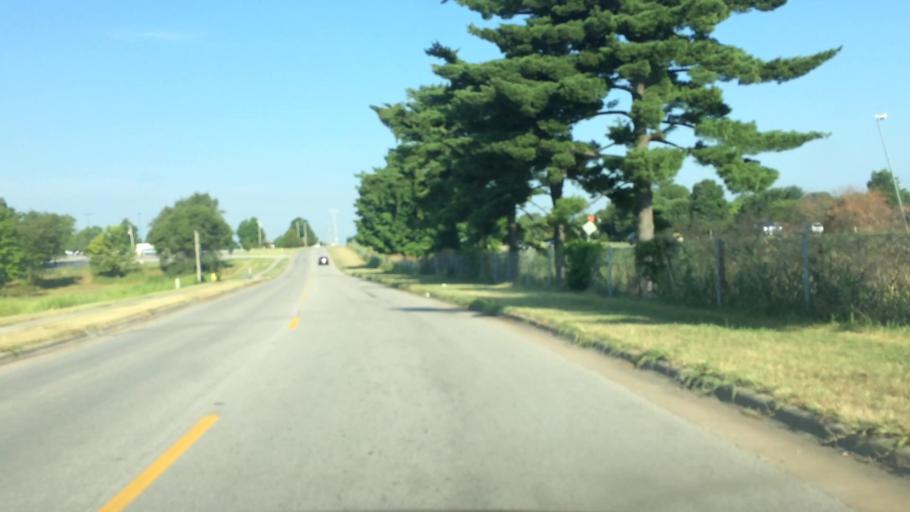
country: US
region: Missouri
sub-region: Greene County
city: Springfield
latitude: 37.2498
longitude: -93.2664
